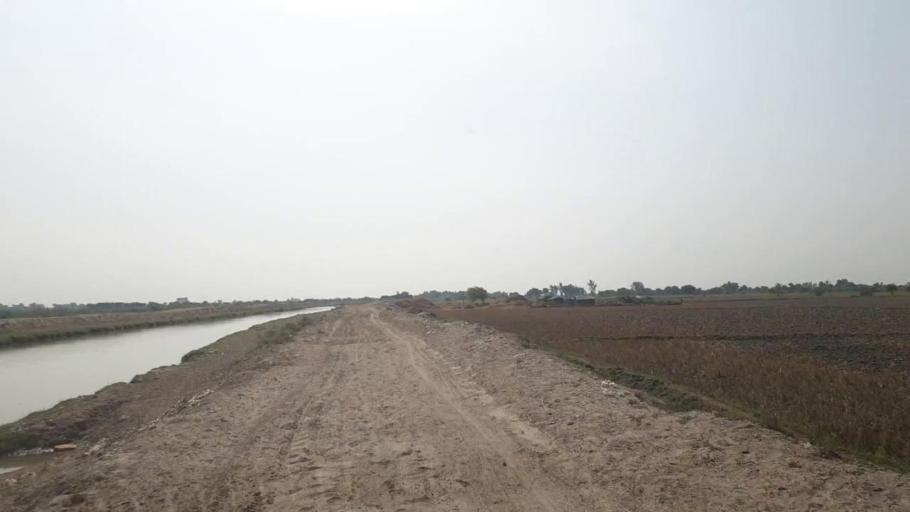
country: PK
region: Sindh
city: Badin
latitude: 24.5487
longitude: 68.8499
